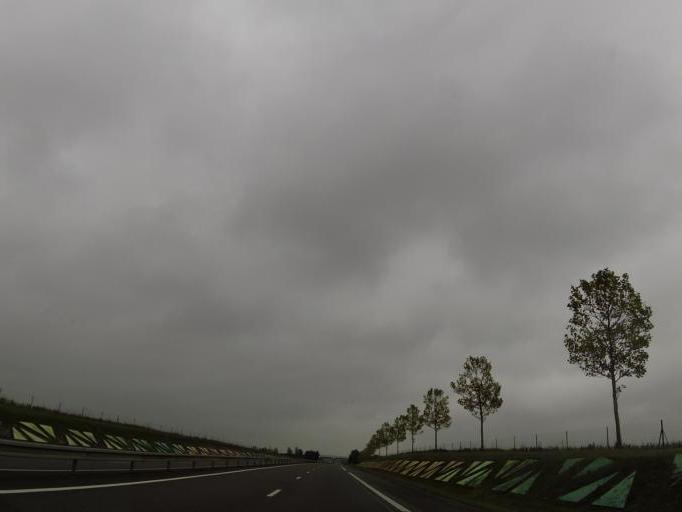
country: FR
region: Champagne-Ardenne
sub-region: Departement de la Marne
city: Courtisols
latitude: 49.0289
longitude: 4.4917
